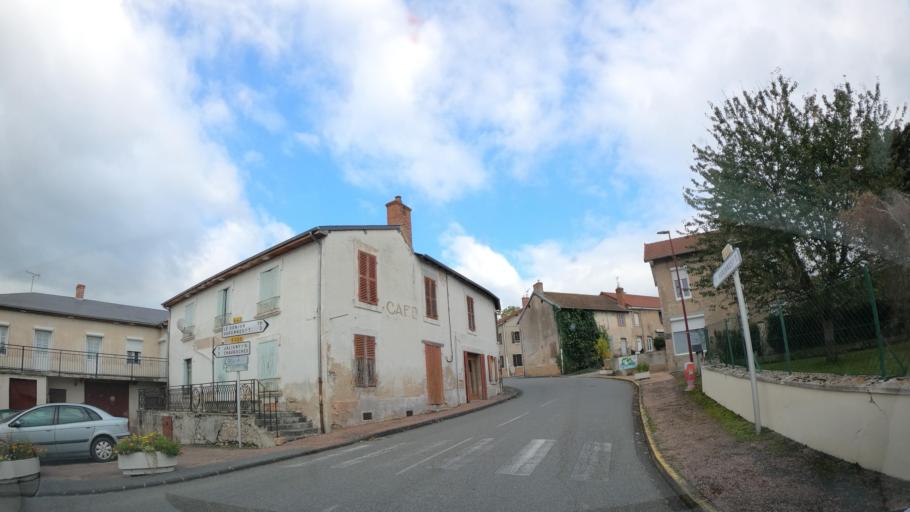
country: FR
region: Auvergne
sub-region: Departement de l'Allier
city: Lapalisse
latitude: 46.3286
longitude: 3.5933
